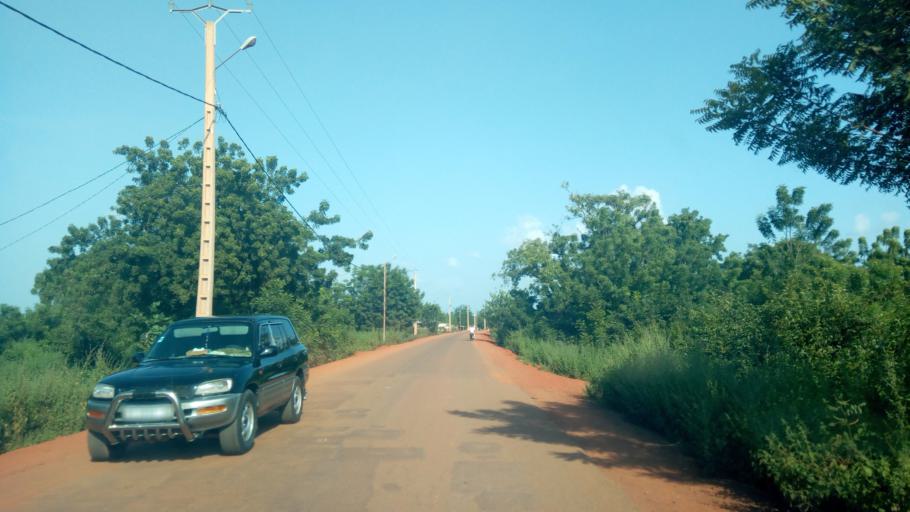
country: ML
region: Sikasso
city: Yorosso
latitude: 12.1848
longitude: -4.8136
